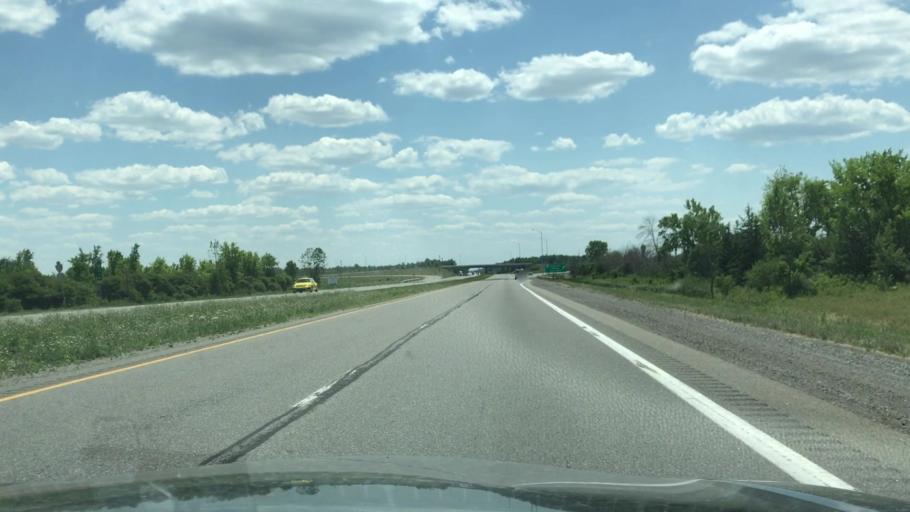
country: US
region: New York
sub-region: Niagara County
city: Niagara Falls
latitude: 42.9947
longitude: -79.0631
